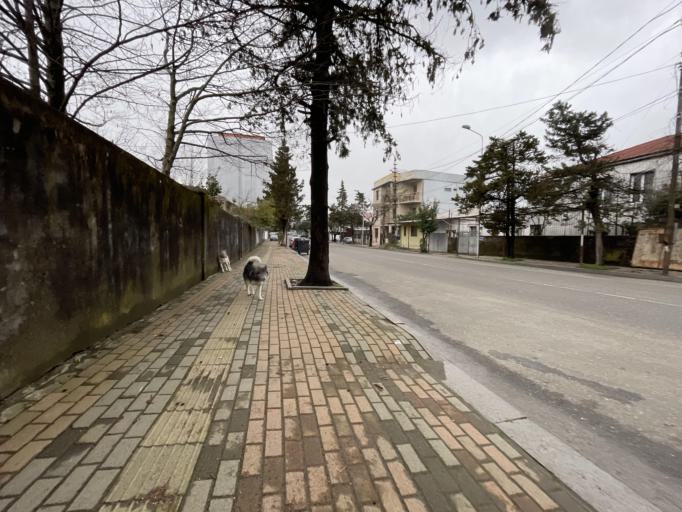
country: GE
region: Ajaria
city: Batumi
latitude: 41.6359
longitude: 41.6455
